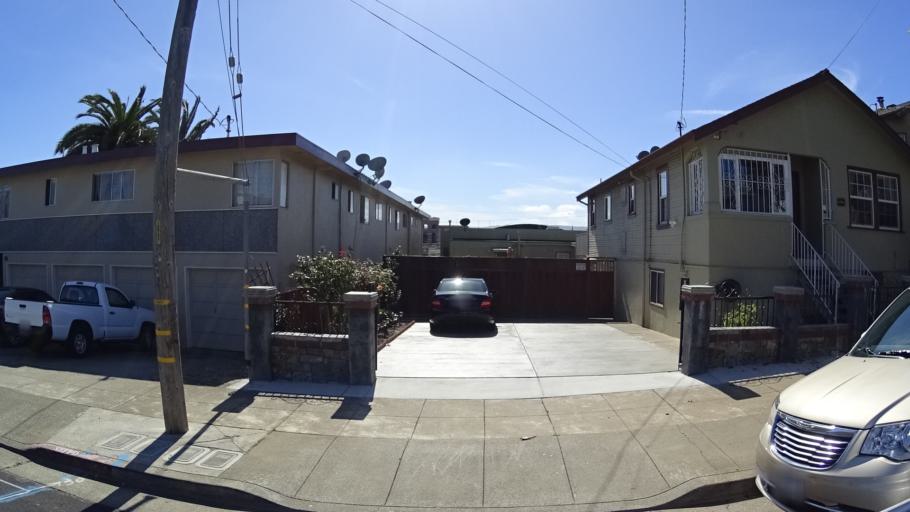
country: US
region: California
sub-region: San Mateo County
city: South San Francisco
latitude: 37.6583
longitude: -122.4104
